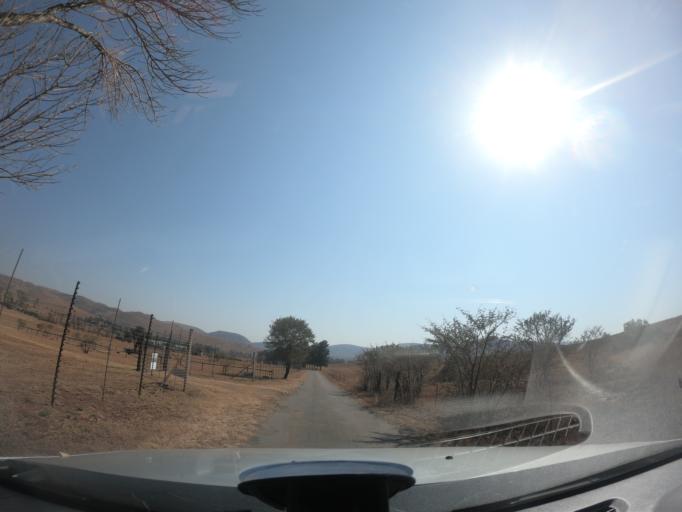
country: ZA
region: Gauteng
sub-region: City of Johannesburg Metropolitan Municipality
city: Diepsloot
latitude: -25.8377
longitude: 28.0313
